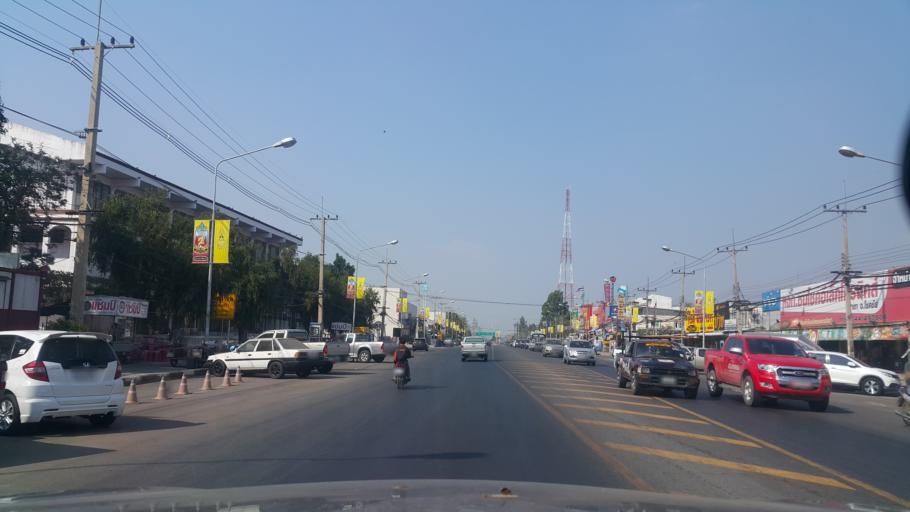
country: TH
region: Nakhon Ratchasima
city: Chok Chai
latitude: 14.7345
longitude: 102.1655
